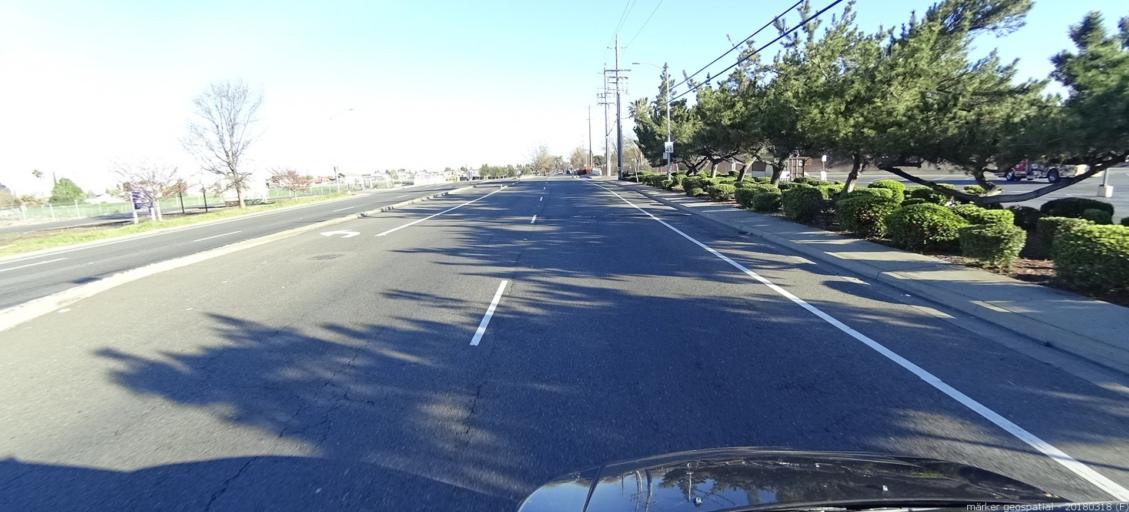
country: US
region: California
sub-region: Sacramento County
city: Parkway
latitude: 38.4752
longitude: -121.4506
